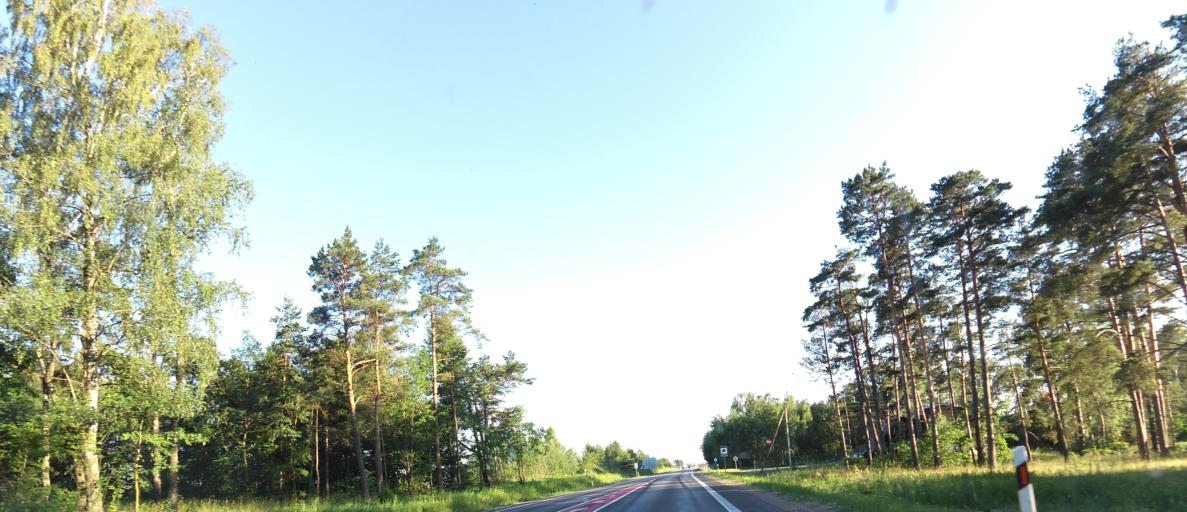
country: LT
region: Panevezys
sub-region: Panevezys City
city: Panevezys
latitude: 55.6560
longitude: 24.3581
